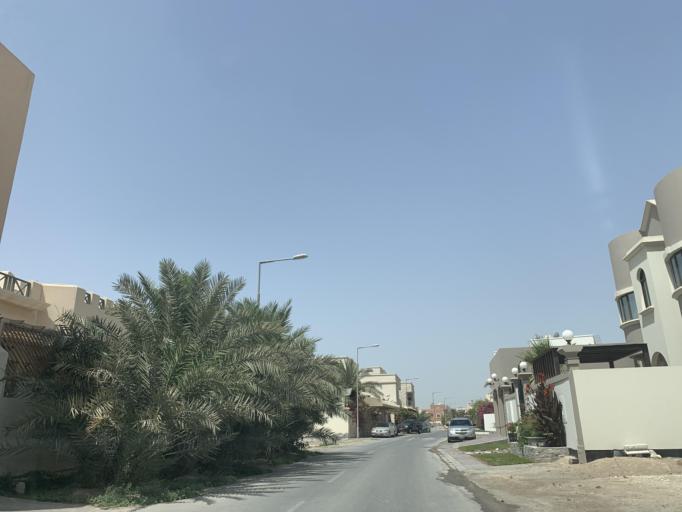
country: BH
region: Northern
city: Sitrah
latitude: 26.1561
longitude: 50.5887
